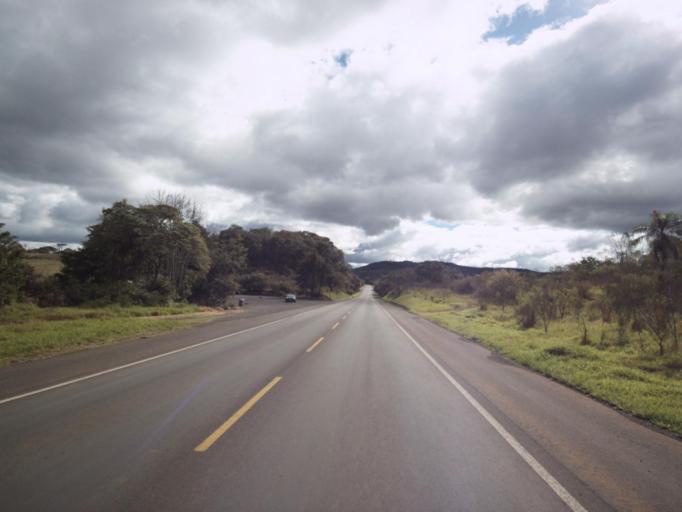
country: BR
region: Santa Catarina
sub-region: Concordia
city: Concordia
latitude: -27.3337
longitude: -51.9762
